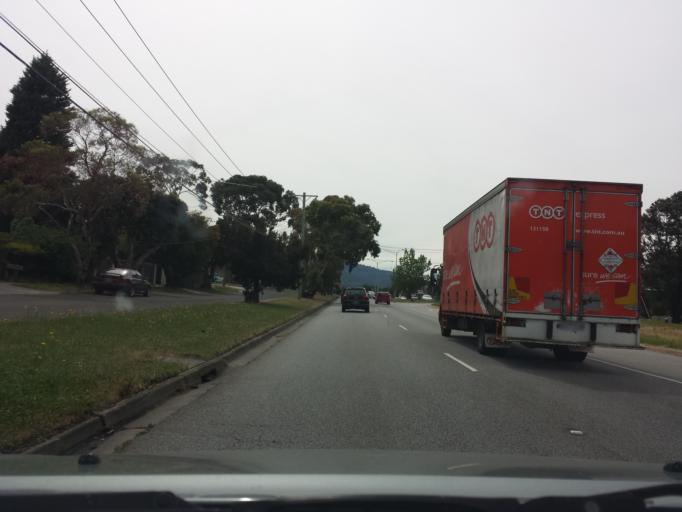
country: AU
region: Victoria
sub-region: Knox
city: Scoresby
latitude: -37.8981
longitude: 145.2385
